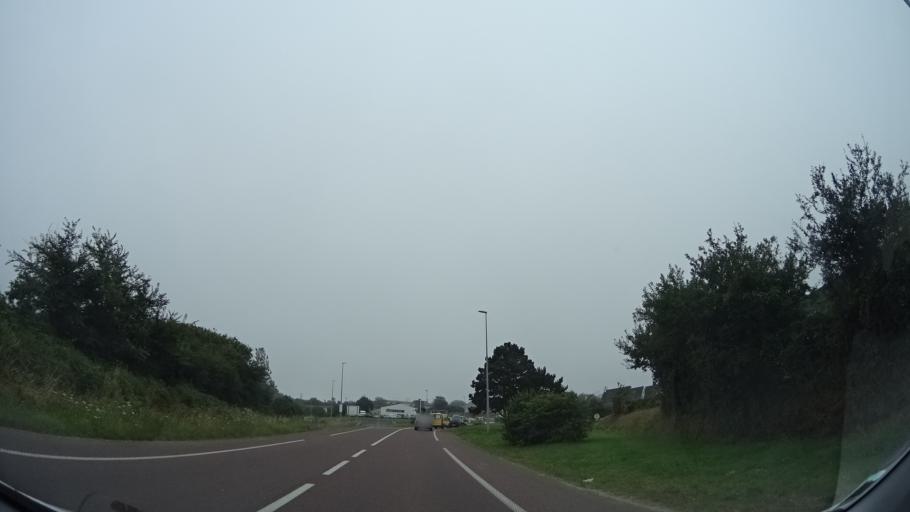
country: FR
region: Lower Normandy
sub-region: Departement de la Manche
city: Les Pieux
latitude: 49.5186
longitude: -1.8128
